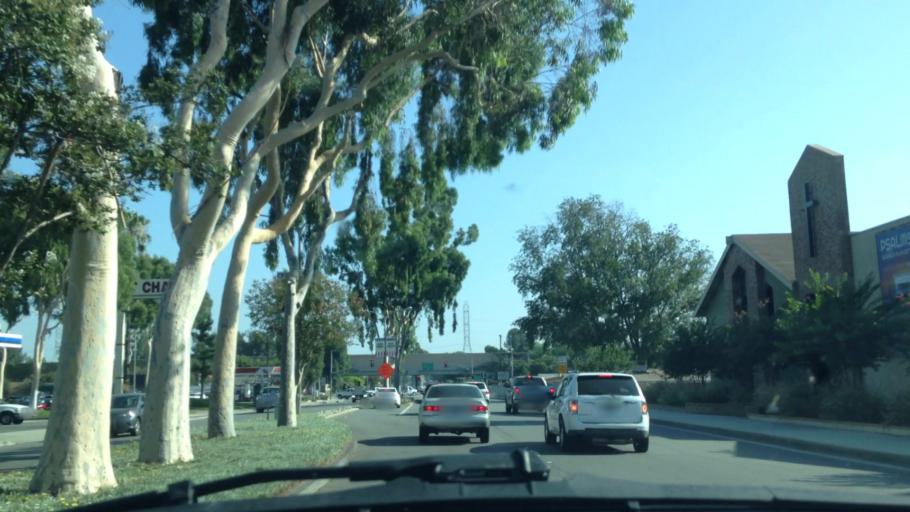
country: US
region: California
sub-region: Los Angeles County
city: Glendora
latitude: 34.1233
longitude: -117.8727
